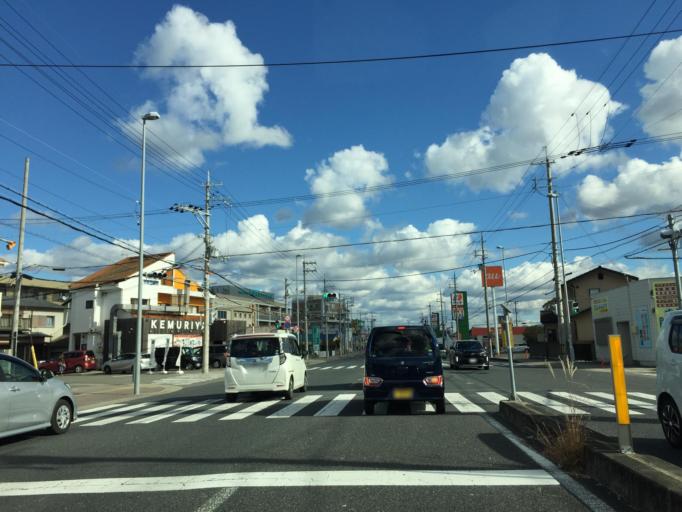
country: JP
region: Wakayama
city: Wakayama-shi
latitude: 34.2612
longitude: 135.1845
